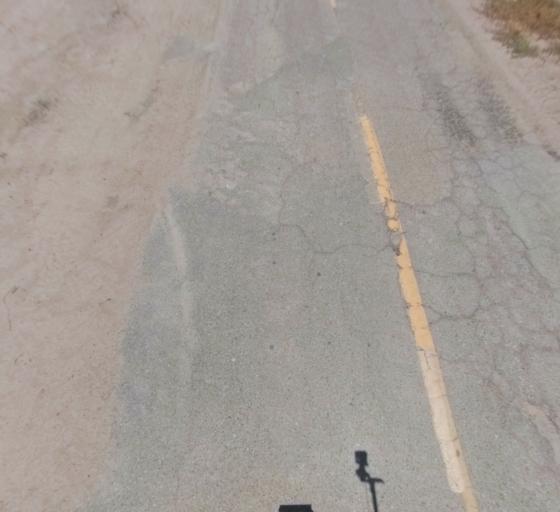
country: US
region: California
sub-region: Madera County
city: Parkwood
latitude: 36.8710
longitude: -120.0741
